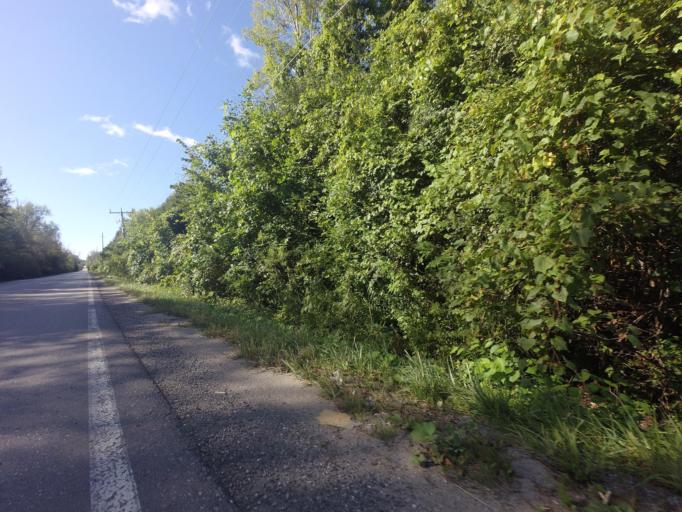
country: CA
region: Ontario
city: Bradford West Gwillimbury
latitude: 44.0540
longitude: -79.5591
